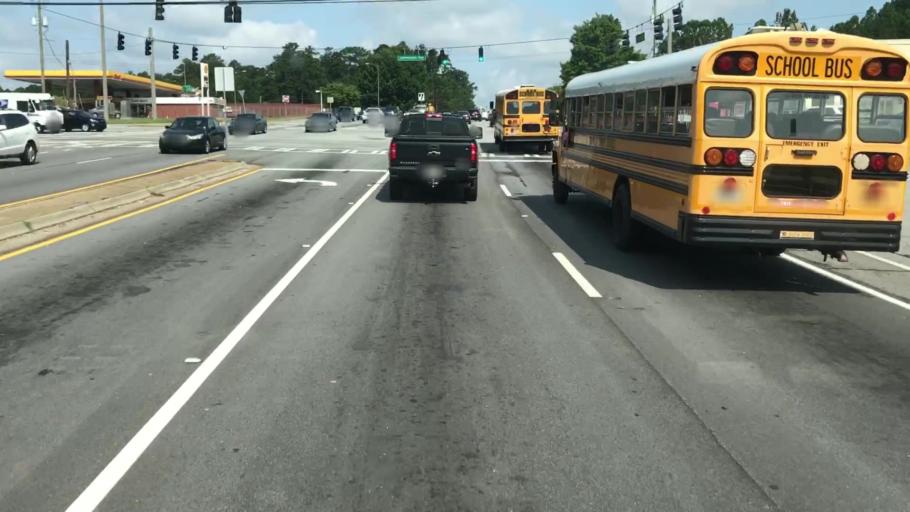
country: US
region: Georgia
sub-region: Gwinnett County
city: Lawrenceville
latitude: 33.9381
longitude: -84.0334
